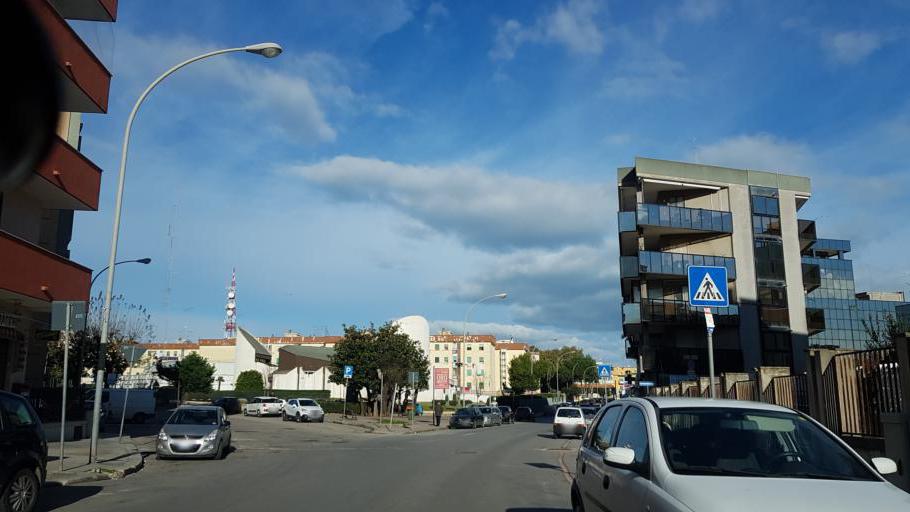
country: IT
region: Apulia
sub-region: Provincia di Brindisi
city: Brindisi
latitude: 40.6230
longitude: 17.9316
